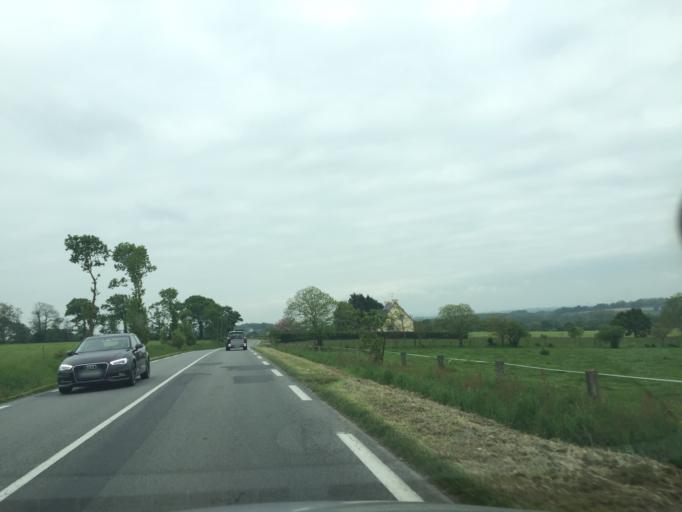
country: FR
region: Brittany
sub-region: Departement des Cotes-d'Armor
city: Lamballe
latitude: 48.4869
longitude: -2.4860
